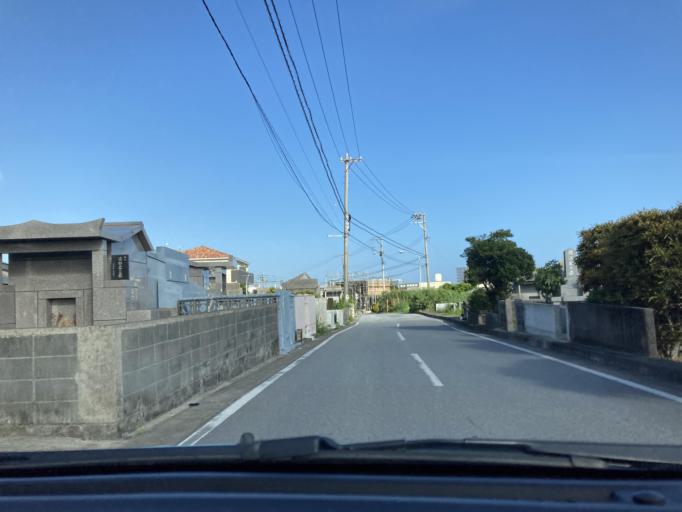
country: JP
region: Okinawa
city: Naha-shi
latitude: 26.2046
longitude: 127.7113
